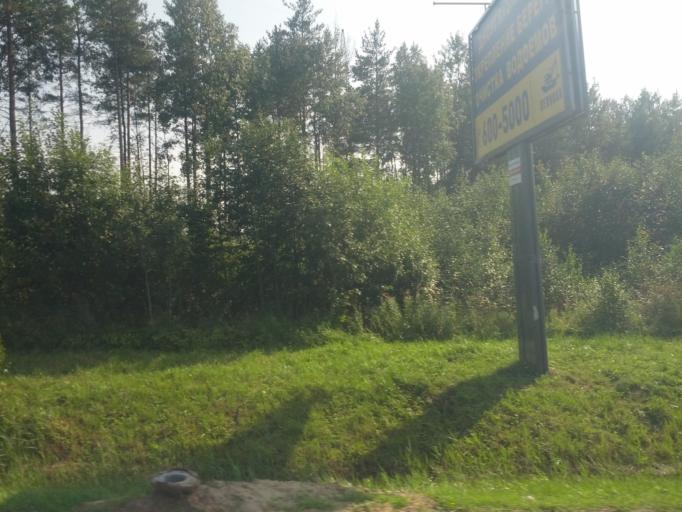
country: RU
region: Leningrad
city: Yanino Vtoroye
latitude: 59.8911
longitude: 30.5586
